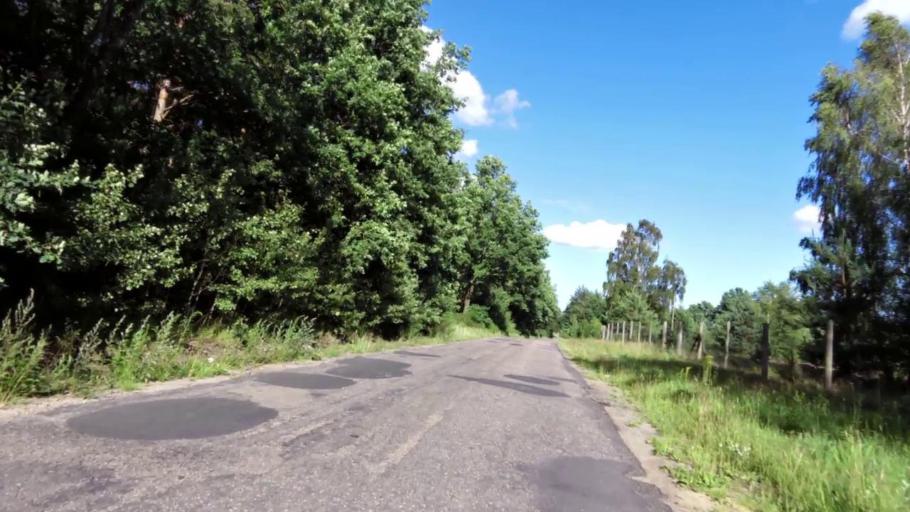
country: PL
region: West Pomeranian Voivodeship
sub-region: Powiat slawienski
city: Slawno
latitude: 54.4365
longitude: 16.7578
